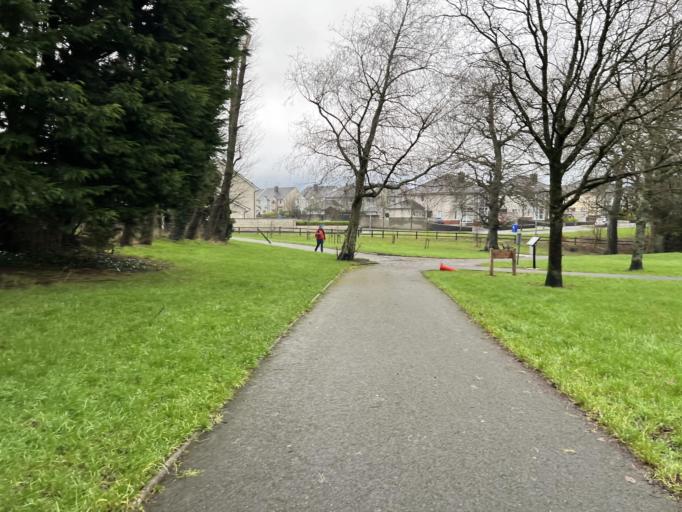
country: IE
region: Connaught
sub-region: County Galway
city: Tuam
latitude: 53.5210
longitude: -8.8500
